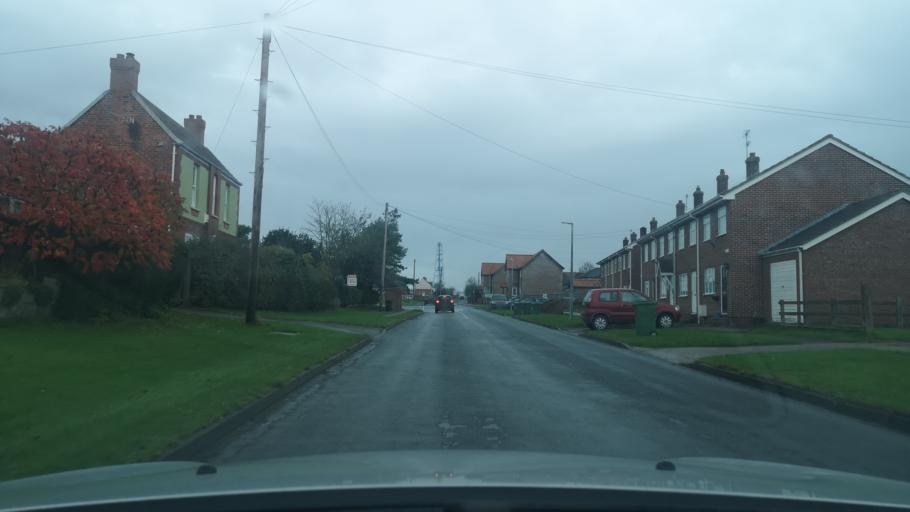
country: GB
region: England
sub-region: East Riding of Yorkshire
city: Easington
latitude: 53.6513
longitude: 0.1141
